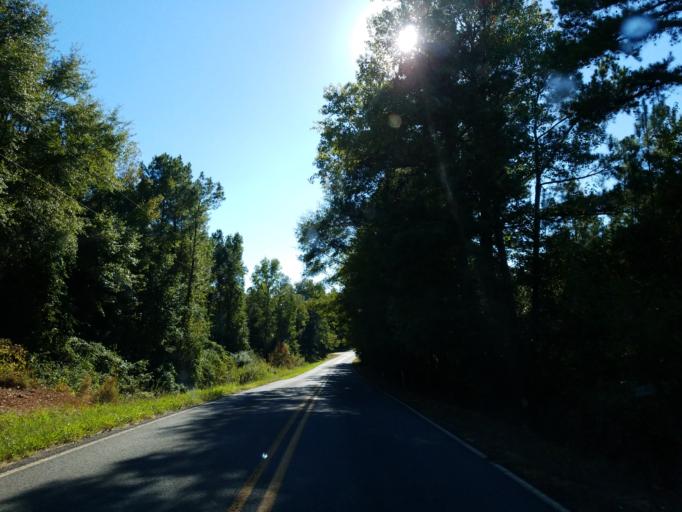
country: US
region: Georgia
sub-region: Dooly County
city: Vienna
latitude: 32.2176
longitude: -83.8871
